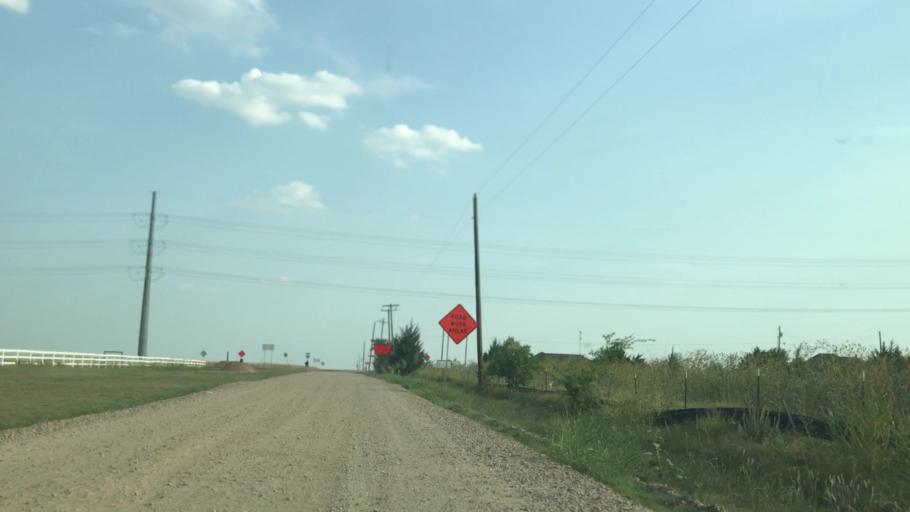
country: US
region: Texas
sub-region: Rockwall County
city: Fate
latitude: 32.9378
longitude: -96.4009
